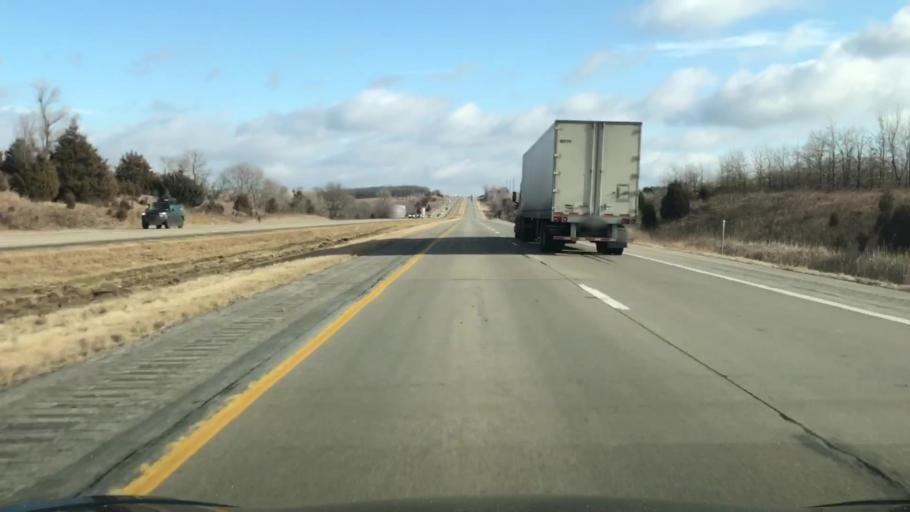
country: US
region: Iowa
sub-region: Cass County
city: Atlantic
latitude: 41.4972
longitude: -94.9059
